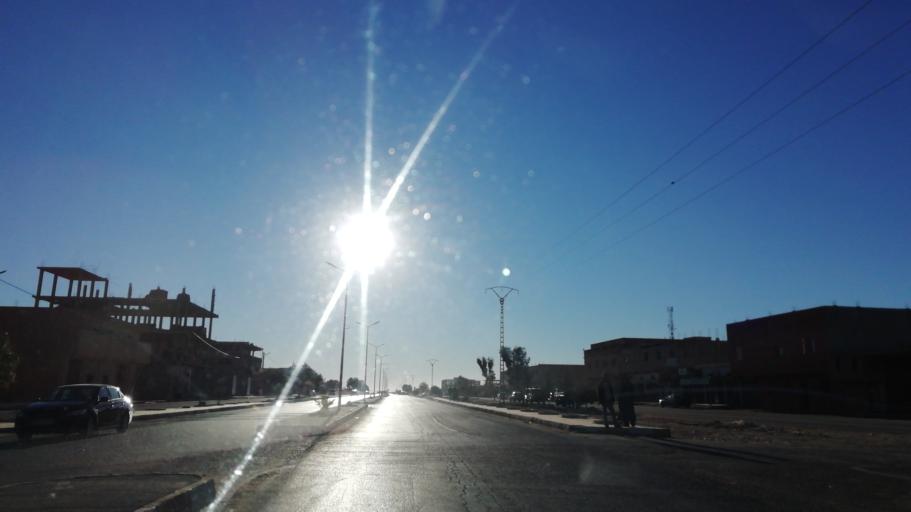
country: DZ
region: Saida
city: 'Ain el Hadjar
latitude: 34.0292
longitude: 0.0927
